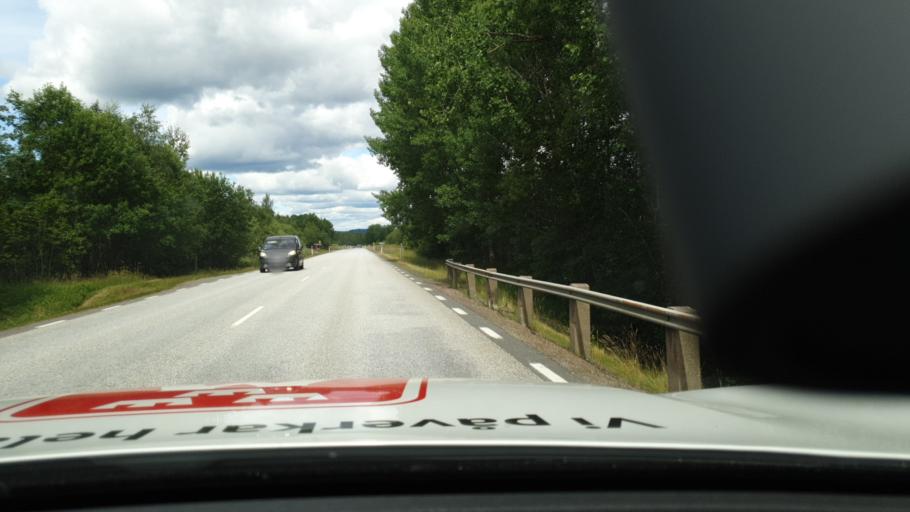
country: SE
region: Vaermland
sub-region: Storfors Kommun
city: Storfors
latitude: 59.5275
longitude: 14.2975
